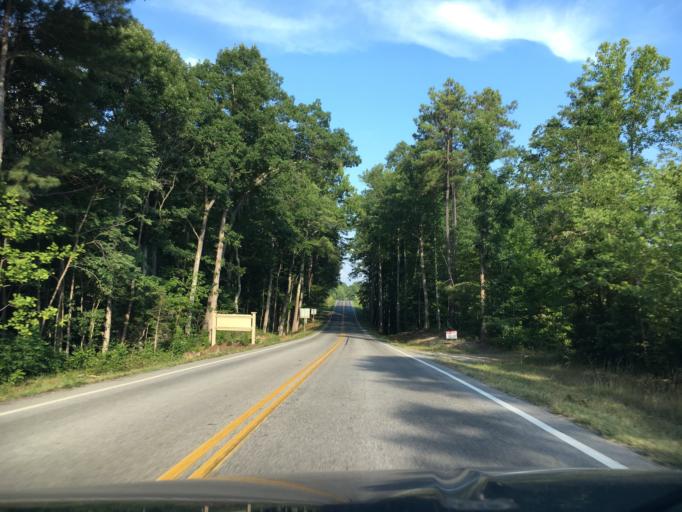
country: US
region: Virginia
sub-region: Franklin County
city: Union Hall
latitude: 36.9757
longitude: -79.6142
